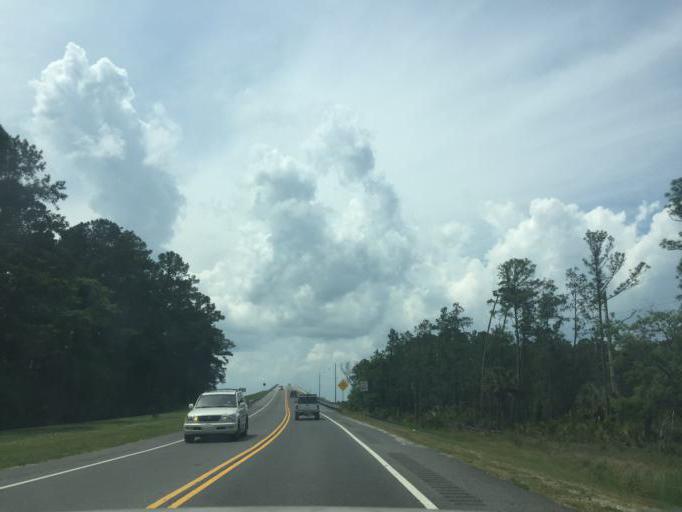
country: US
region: Georgia
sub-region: Chatham County
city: Skidaway Island
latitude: 31.9437
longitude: -81.0609
